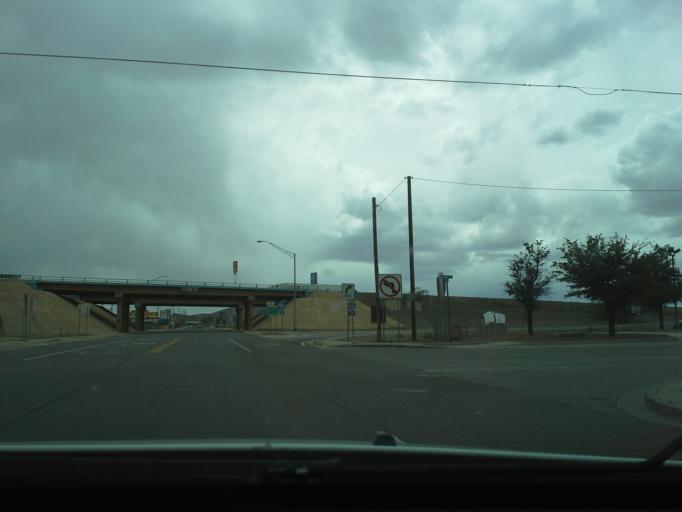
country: US
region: New Mexico
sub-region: Hidalgo County
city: Lordsburg
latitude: 32.3433
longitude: -108.7119
